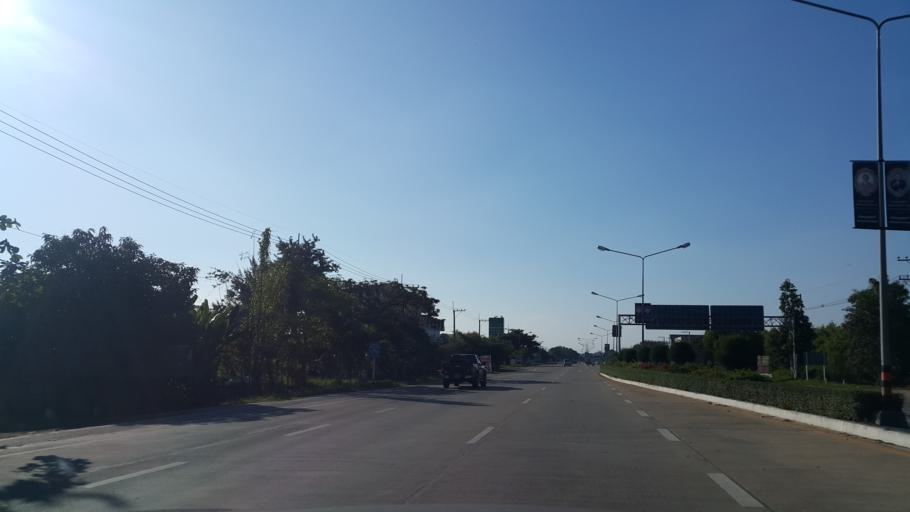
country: TH
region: Lamphun
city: Lamphun
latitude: 18.5718
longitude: 99.0167
